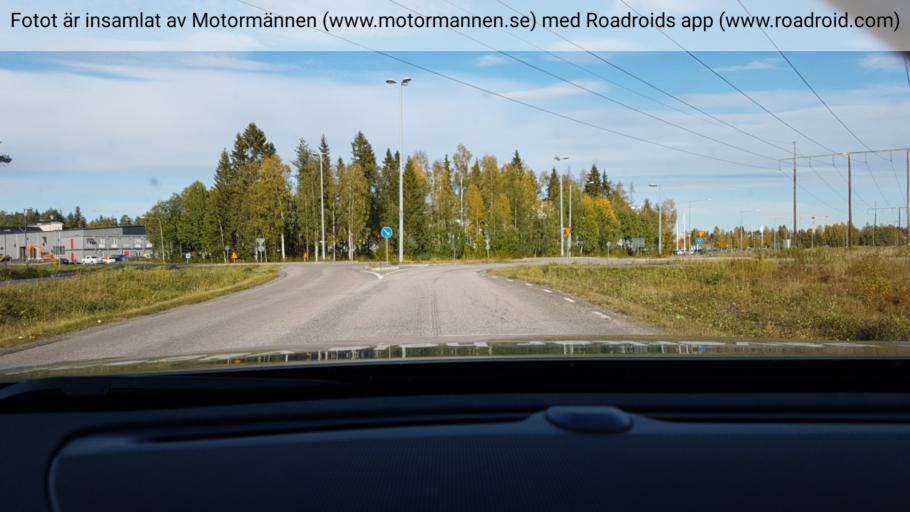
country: SE
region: Norrbotten
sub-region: Lulea Kommun
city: Bergnaset
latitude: 65.6146
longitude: 22.1217
